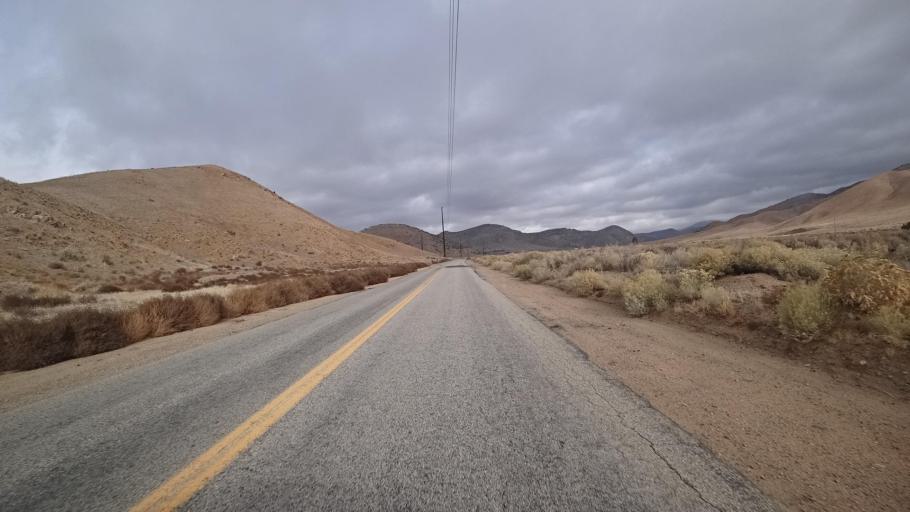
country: US
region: California
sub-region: Kern County
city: Tehachapi
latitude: 35.1151
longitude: -118.3235
